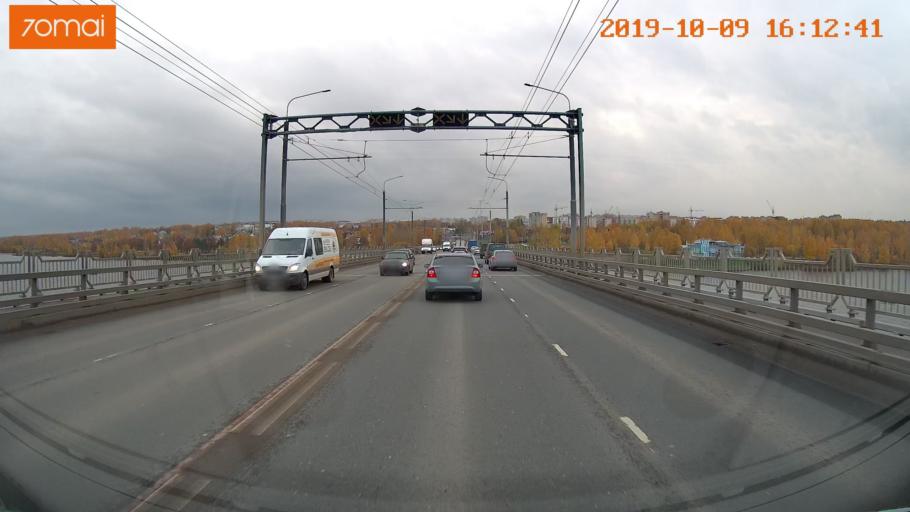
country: RU
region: Kostroma
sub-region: Kostromskoy Rayon
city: Kostroma
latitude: 57.7509
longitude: 40.9361
